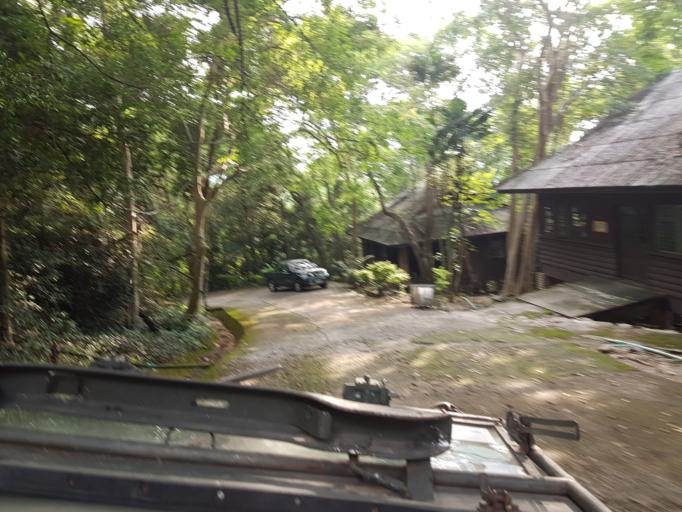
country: TH
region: Pattani
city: Khok Pho
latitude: 6.6584
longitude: 101.0961
